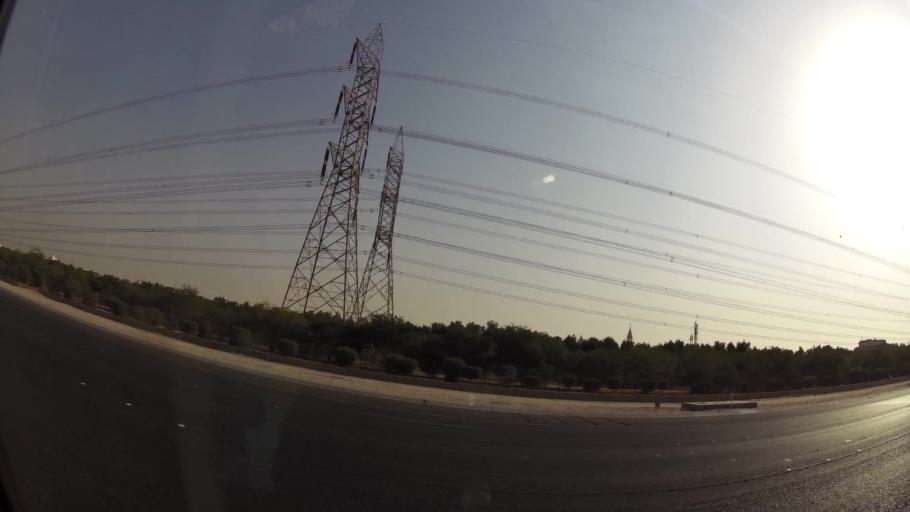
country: KW
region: Al Asimah
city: Ar Rabiyah
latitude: 29.2978
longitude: 47.8964
